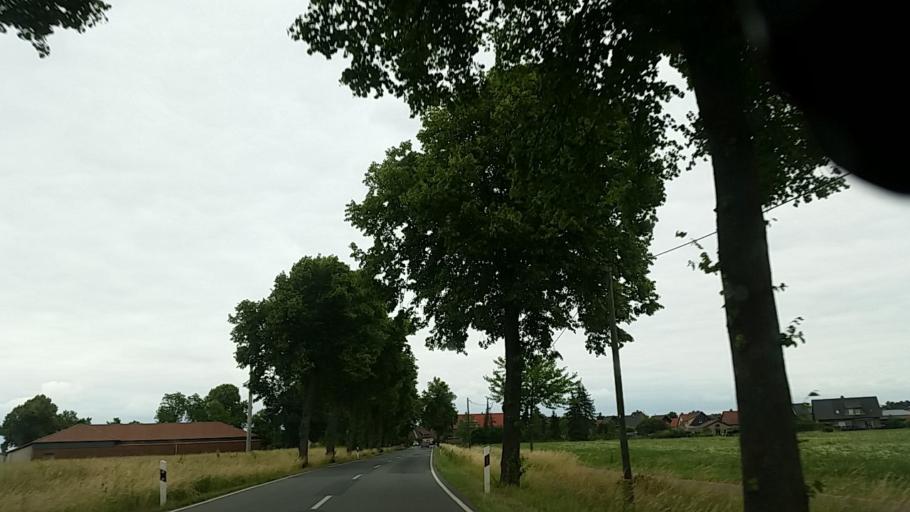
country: DE
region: Lower Saxony
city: Grafhorst
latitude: 52.4417
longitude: 10.9386
